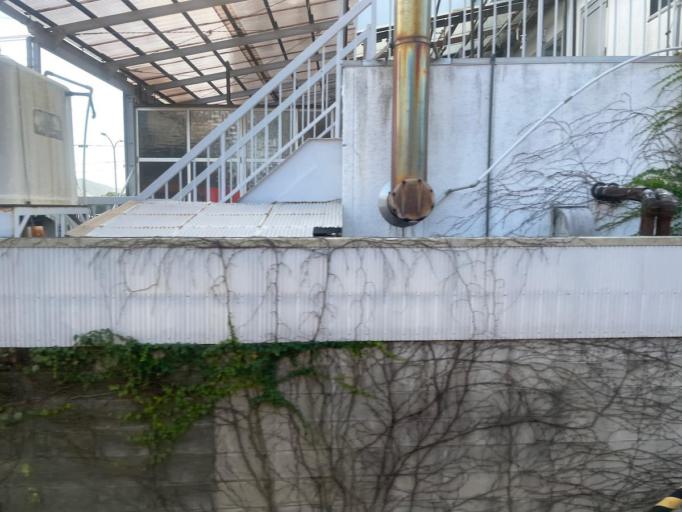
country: JP
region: Mie
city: Toba
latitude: 34.4787
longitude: 136.8454
